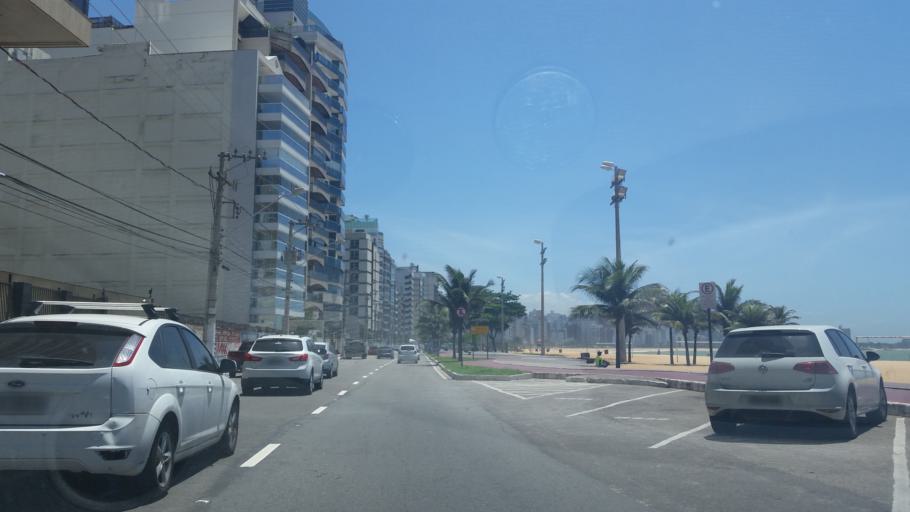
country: BR
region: Espirito Santo
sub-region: Vila Velha
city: Vila Velha
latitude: -20.3485
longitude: -40.2841
